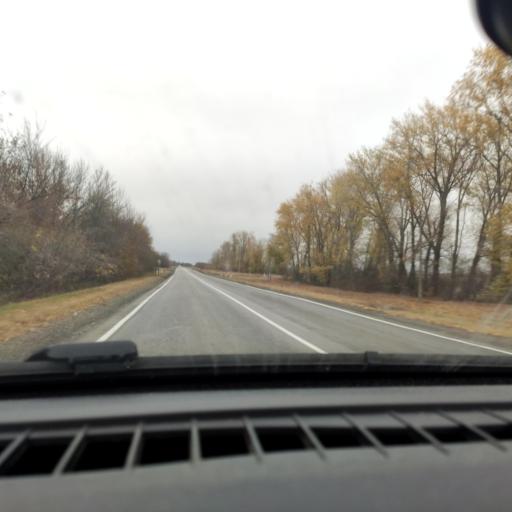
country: RU
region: Voronezj
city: Uryv-Pokrovka
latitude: 51.0890
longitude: 39.0061
